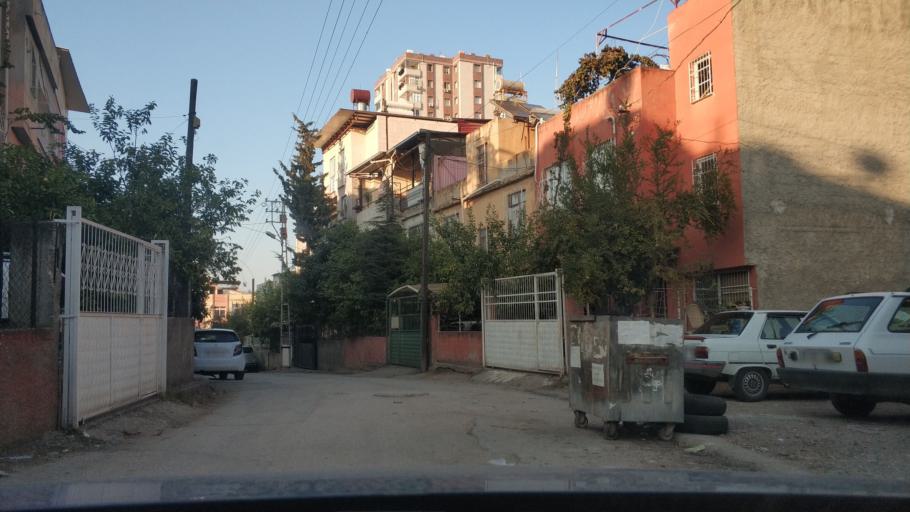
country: TR
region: Adana
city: Seyhan
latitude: 37.0462
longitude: 35.2707
